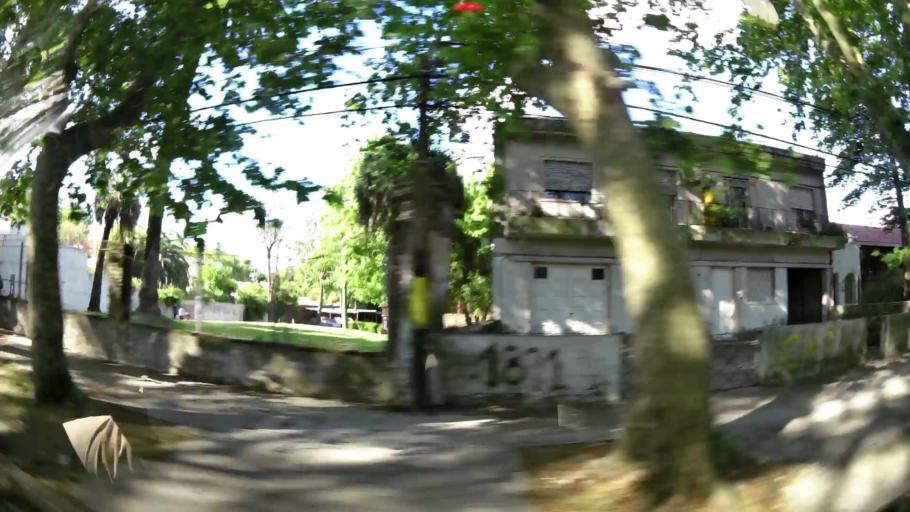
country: UY
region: Montevideo
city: Montevideo
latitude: -34.8586
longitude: -56.1915
